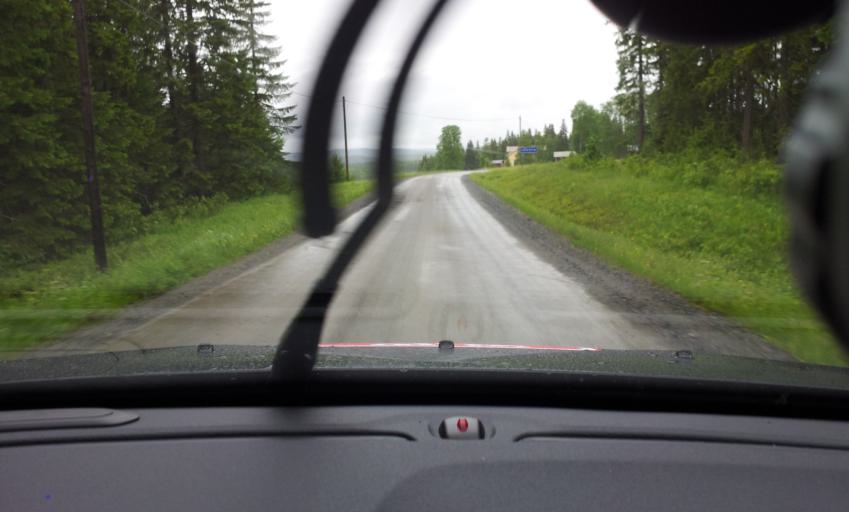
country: SE
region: Jaemtland
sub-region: Are Kommun
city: Are
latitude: 63.4268
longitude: 12.8075
